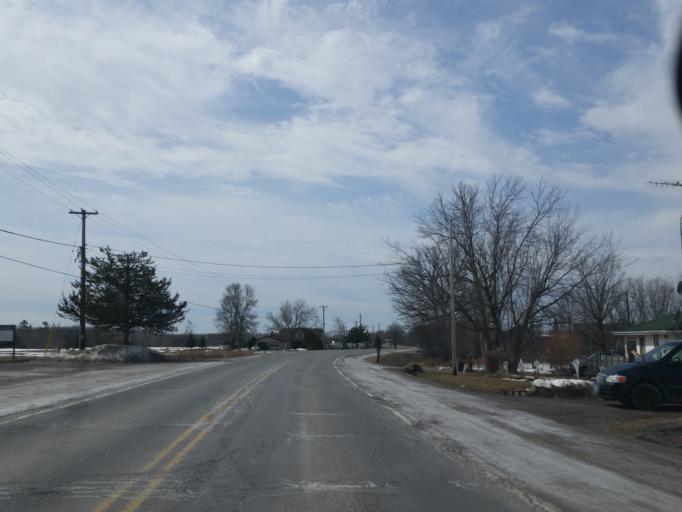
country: CA
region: Ontario
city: Deseronto
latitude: 44.1912
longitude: -77.1155
